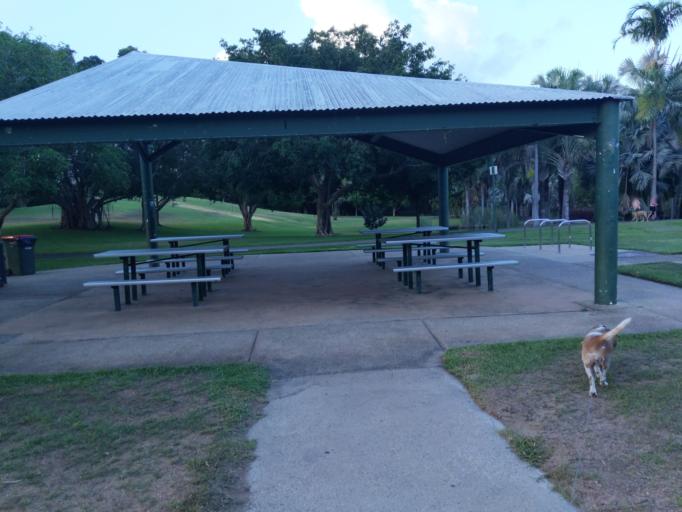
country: AU
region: Northern Territory
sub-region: Darwin
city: Nightcliff
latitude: -12.3873
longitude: 130.8678
